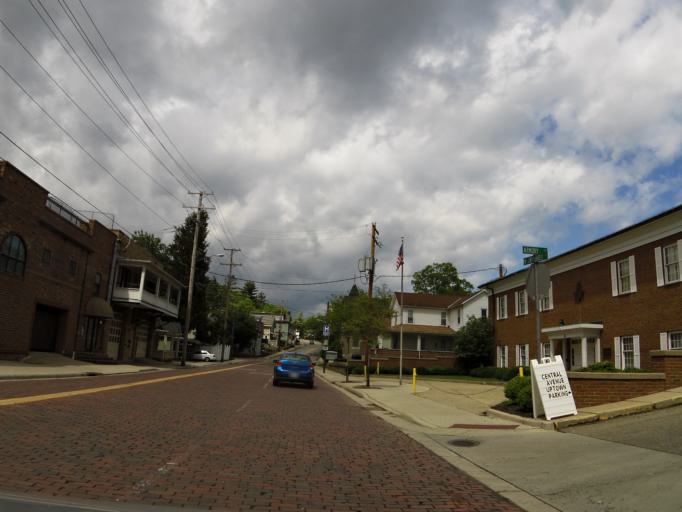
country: US
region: Ohio
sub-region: Athens County
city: Athens
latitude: 39.3323
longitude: -82.1011
